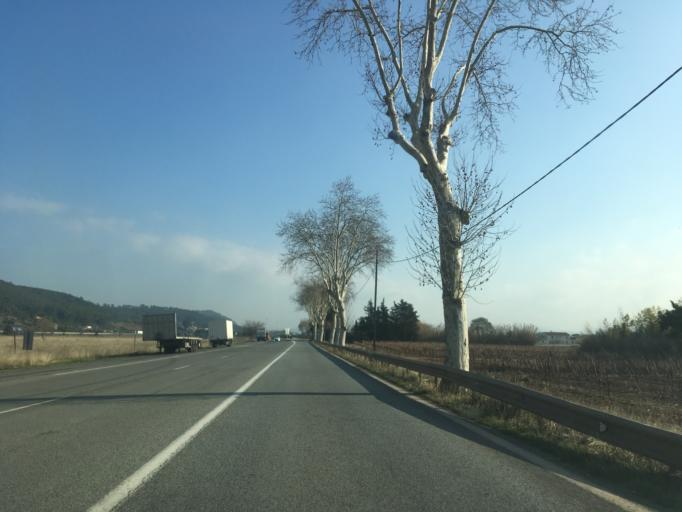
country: FR
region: Provence-Alpes-Cote d'Azur
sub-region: Departement du Var
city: Le Cannet-des-Maures
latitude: 43.3980
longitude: 6.3612
